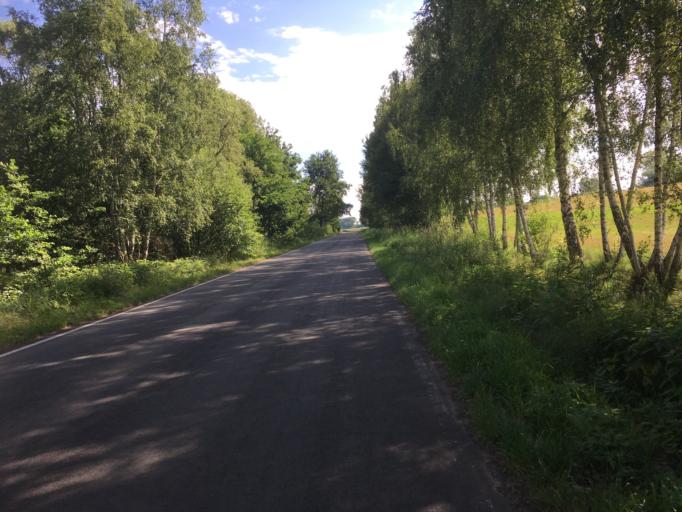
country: DE
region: Brandenburg
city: Drachhausen
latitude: 51.8499
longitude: 14.3015
